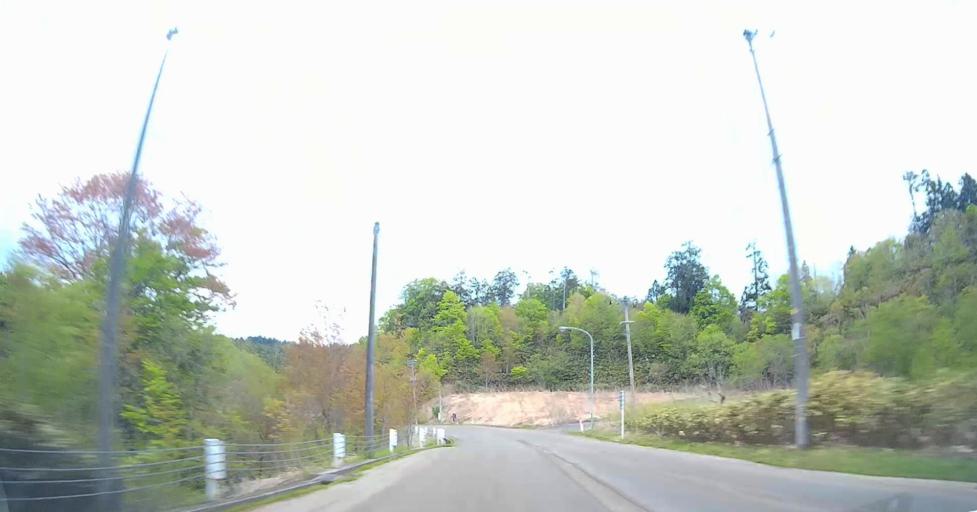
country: JP
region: Aomori
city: Goshogawara
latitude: 41.1019
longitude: 140.5481
